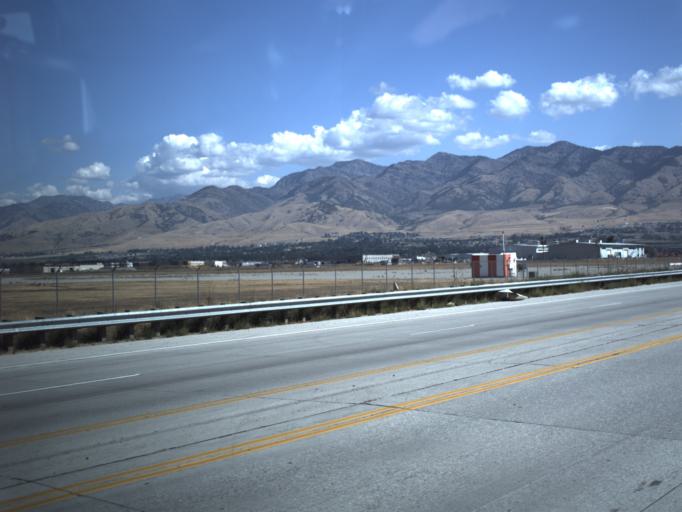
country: US
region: Utah
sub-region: Cache County
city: Hyde Park
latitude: 41.7779
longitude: -111.8517
